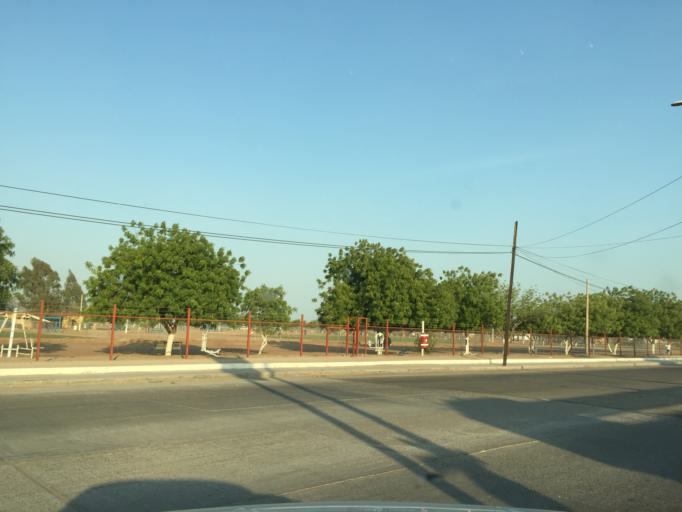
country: MX
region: Sonora
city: Navojoa
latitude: 27.0565
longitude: -109.4555
